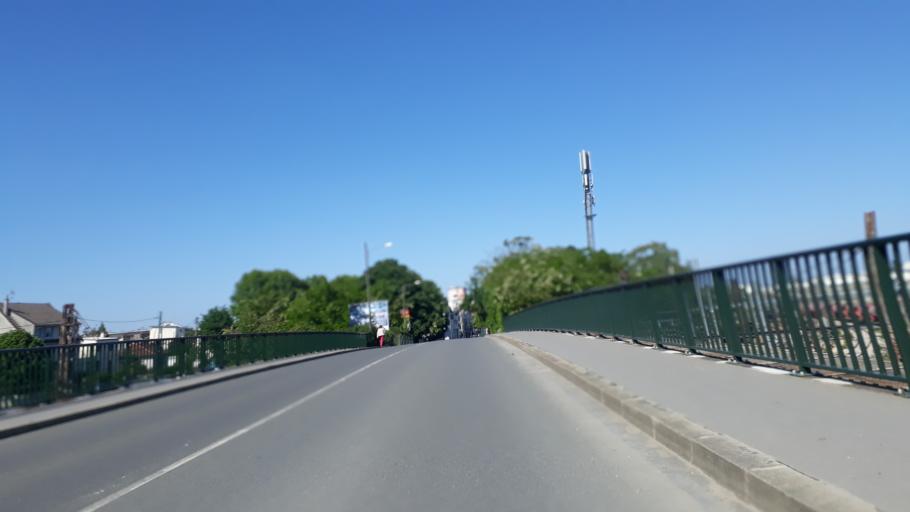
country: FR
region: Ile-de-France
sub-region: Departement de l'Essonne
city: Palaiseau
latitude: 48.7231
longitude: 2.2541
